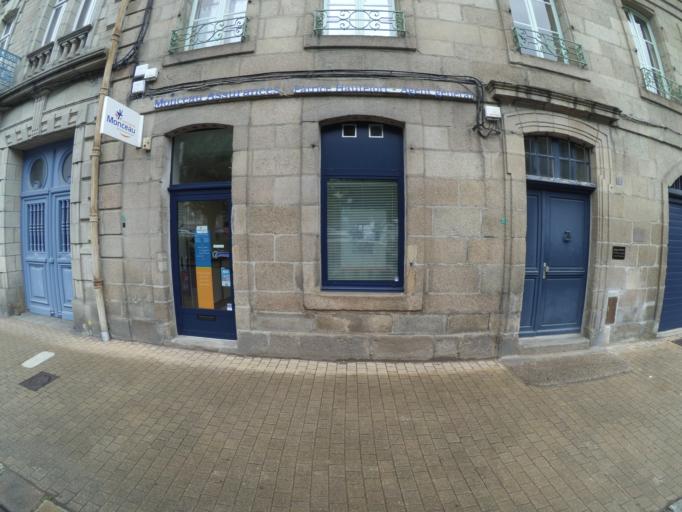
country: FR
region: Brittany
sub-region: Departement du Finistere
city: Morlaix
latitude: 48.5813
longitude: -3.8312
